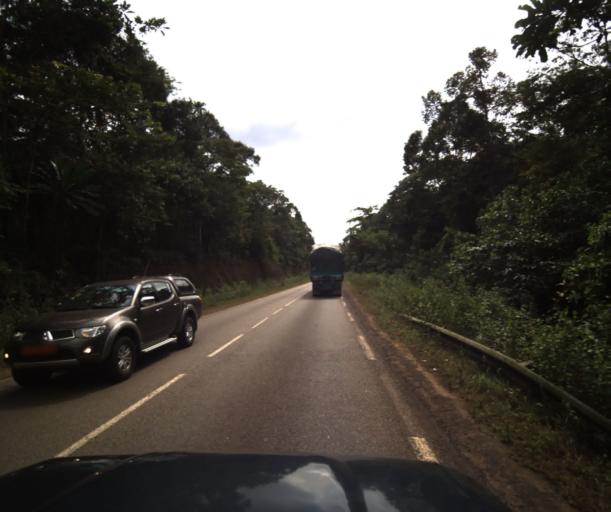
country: CM
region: Littoral
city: Edea
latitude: 3.8150
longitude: 10.3330
